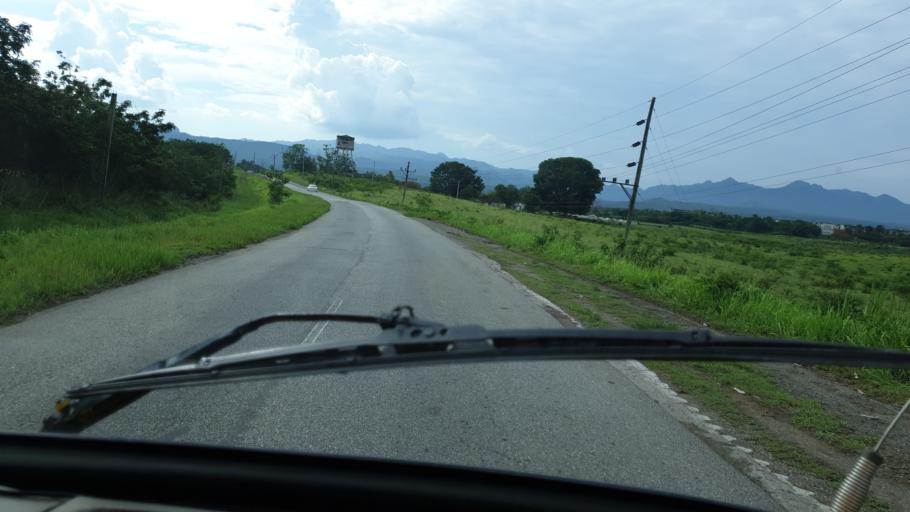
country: CU
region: Cienfuegos
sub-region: Municipio de Cienfuegos
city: Cumanayagua
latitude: 22.0714
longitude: -80.3060
